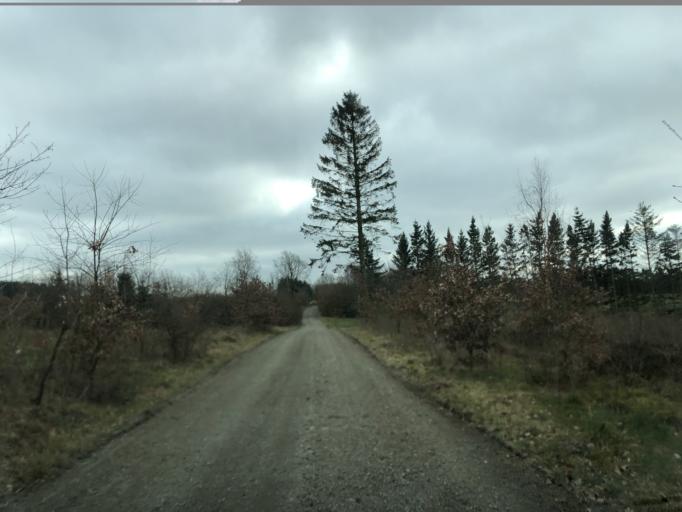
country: DK
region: South Denmark
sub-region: Billund Kommune
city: Billund
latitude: 55.7777
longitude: 9.1795
